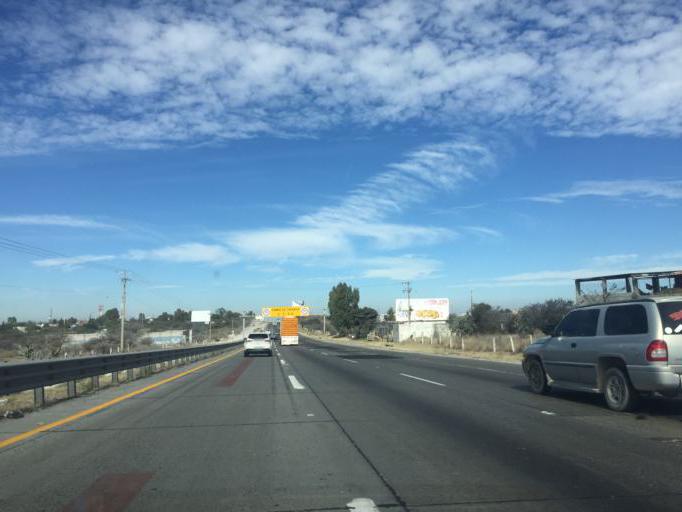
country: MX
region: Queretaro
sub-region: San Juan del Rio
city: Paso de Mata
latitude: 20.3510
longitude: -99.9533
